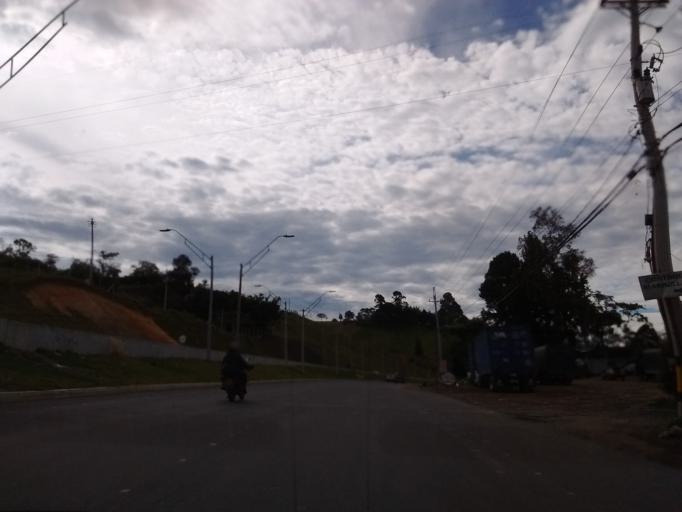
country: CO
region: Antioquia
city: Marinilla
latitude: 6.1594
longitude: -75.3177
